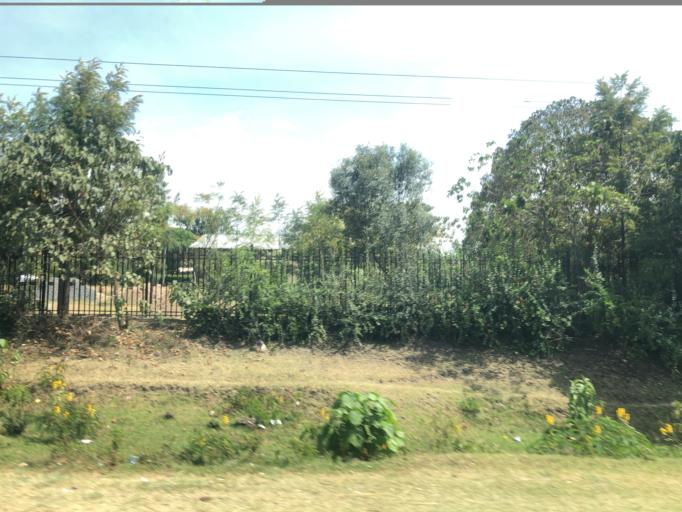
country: ET
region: Oromiya
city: Shashemene
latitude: 7.3108
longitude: 38.6510
